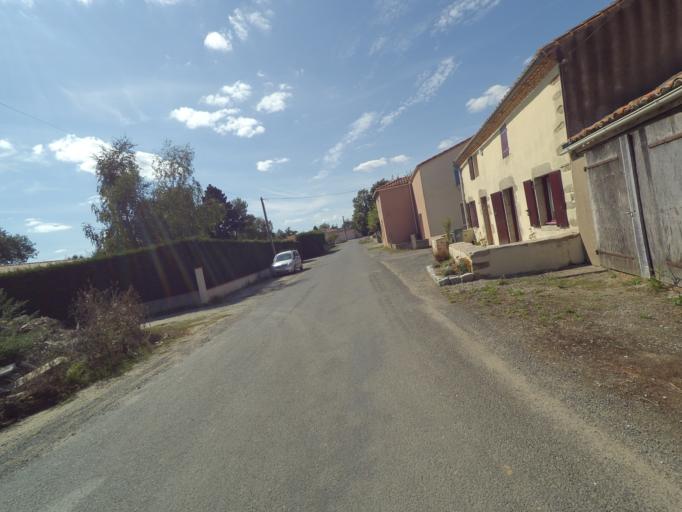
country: FR
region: Pays de la Loire
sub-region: Departement de la Loire-Atlantique
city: Vieillevigne
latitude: 46.9624
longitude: -1.4215
